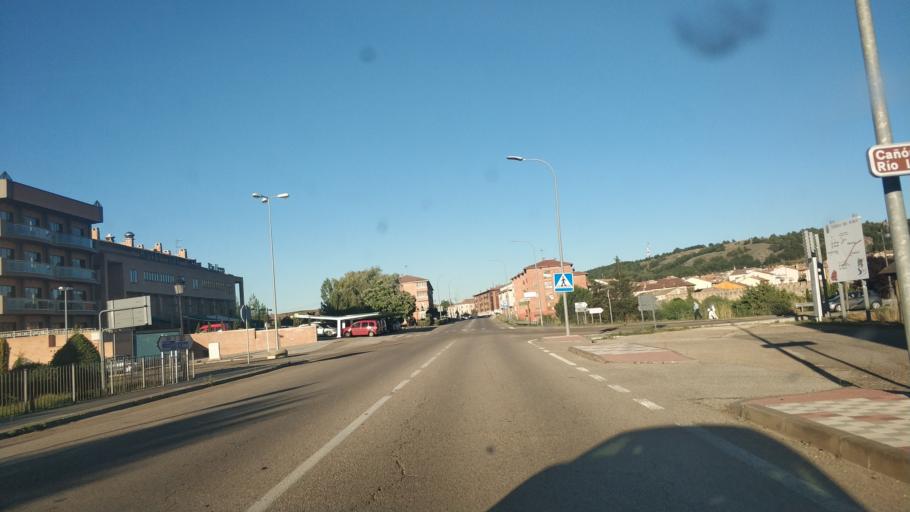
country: ES
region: Castille and Leon
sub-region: Provincia de Soria
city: El Burgo de Osma
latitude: 41.5879
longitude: -3.0734
